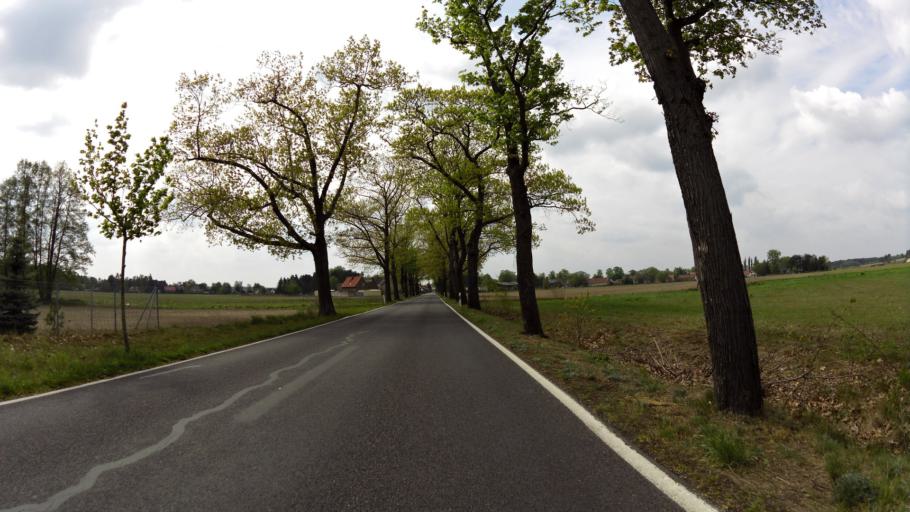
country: DE
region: Brandenburg
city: Bestensee
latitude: 52.2443
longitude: 13.7146
